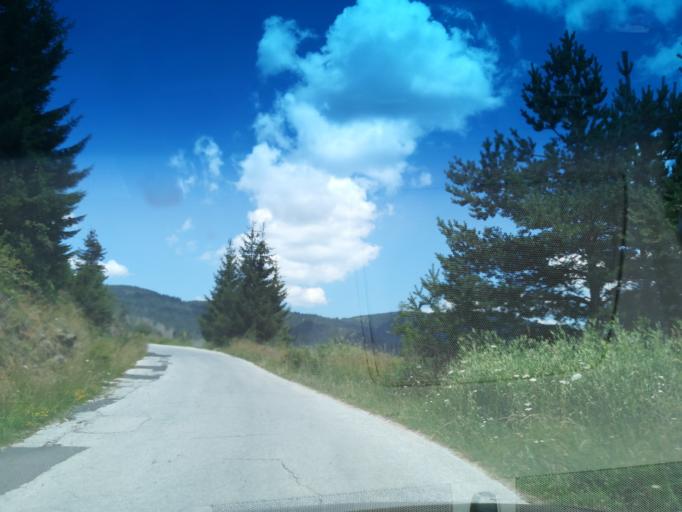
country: BG
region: Smolyan
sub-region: Obshtina Chepelare
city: Chepelare
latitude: 41.6761
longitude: 24.7748
